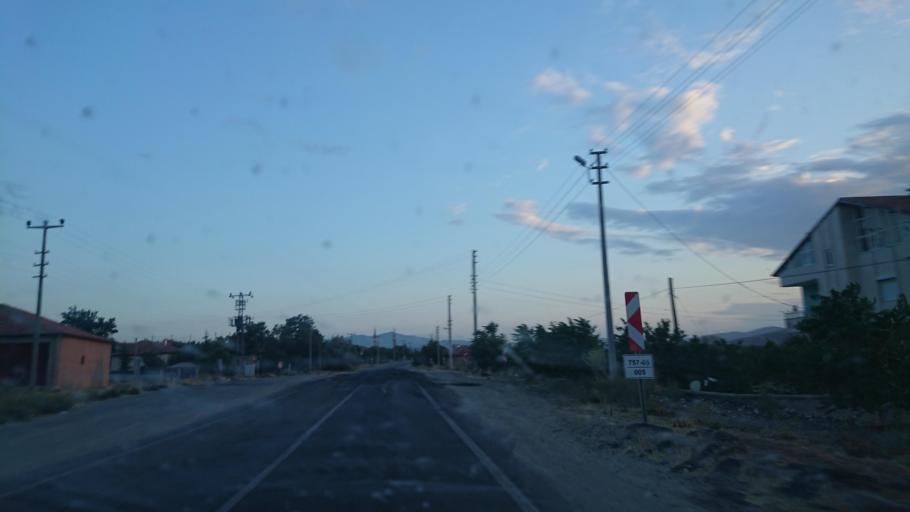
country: TR
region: Aksaray
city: Balci
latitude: 38.7952
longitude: 34.1260
